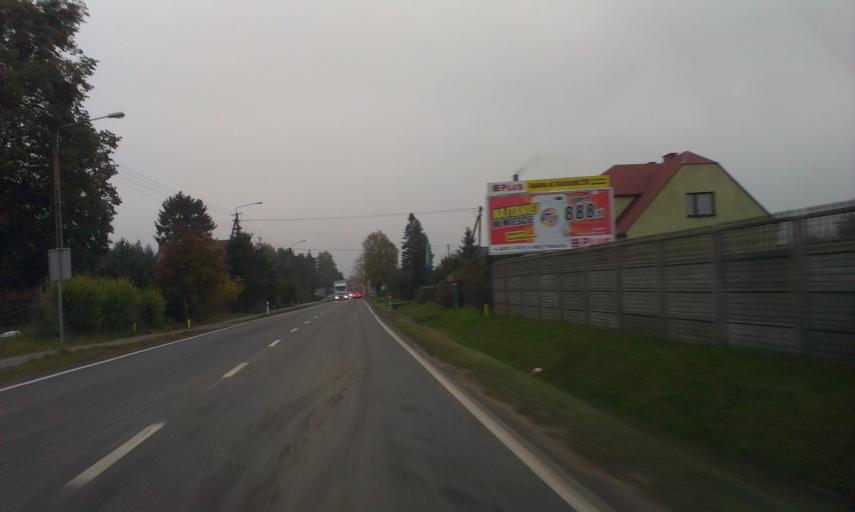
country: PL
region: Kujawsko-Pomorskie
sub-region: Powiat sepolenski
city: Sepolno Krajenskie
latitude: 53.4397
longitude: 17.5433
